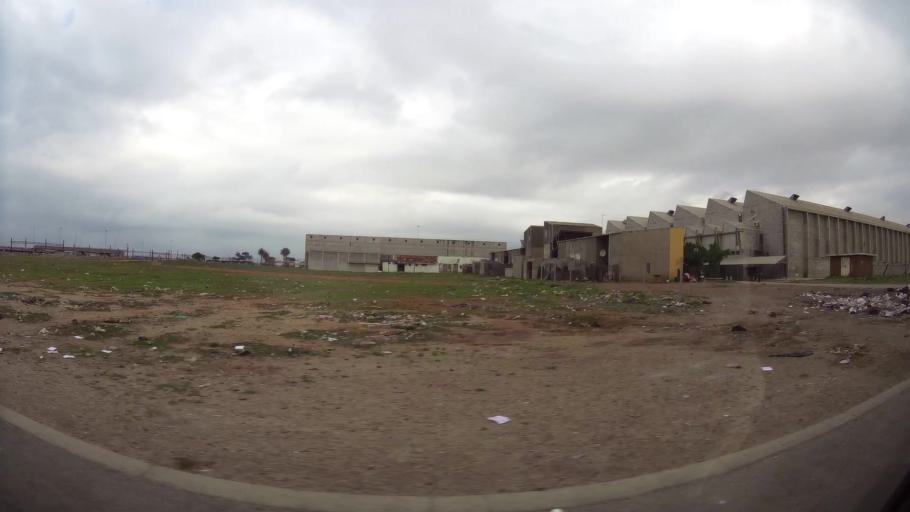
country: ZA
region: Eastern Cape
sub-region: Nelson Mandela Bay Metropolitan Municipality
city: Port Elizabeth
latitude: -33.8970
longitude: 25.6067
